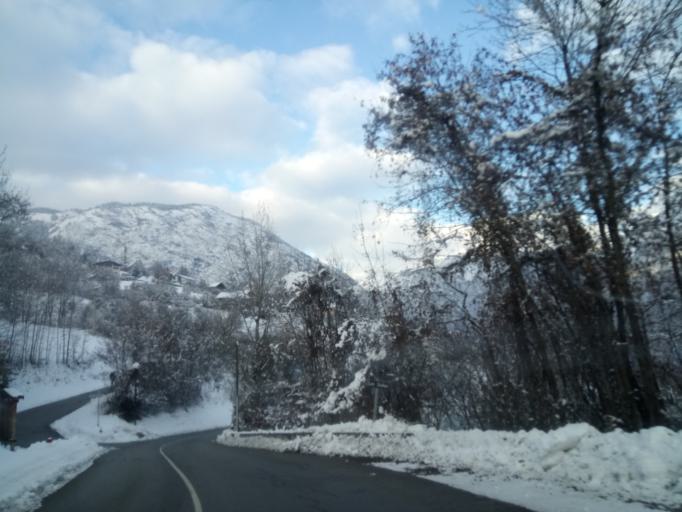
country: FR
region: Rhone-Alpes
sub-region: Departement de la Savoie
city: Saint-Jean-de-Maurienne
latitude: 45.2658
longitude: 6.3305
